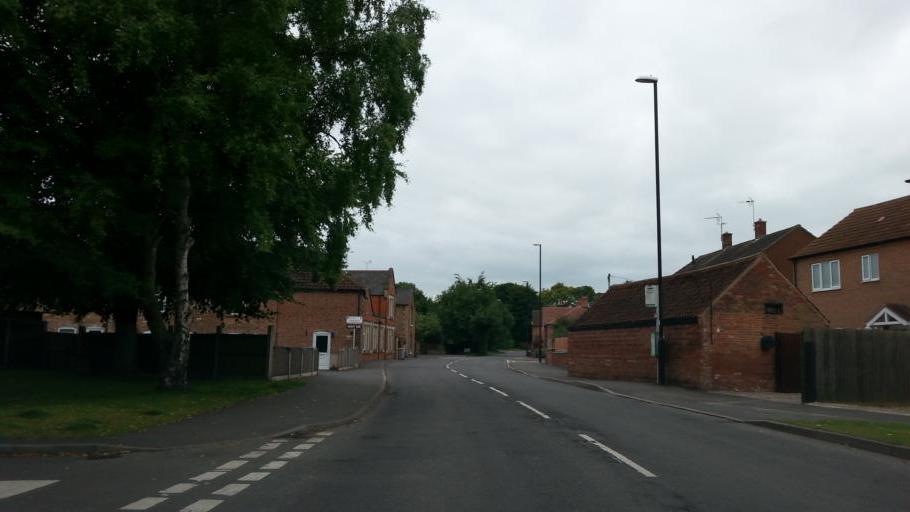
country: GB
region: England
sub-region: Nottinghamshire
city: Southwell
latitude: 53.0773
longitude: -0.9430
